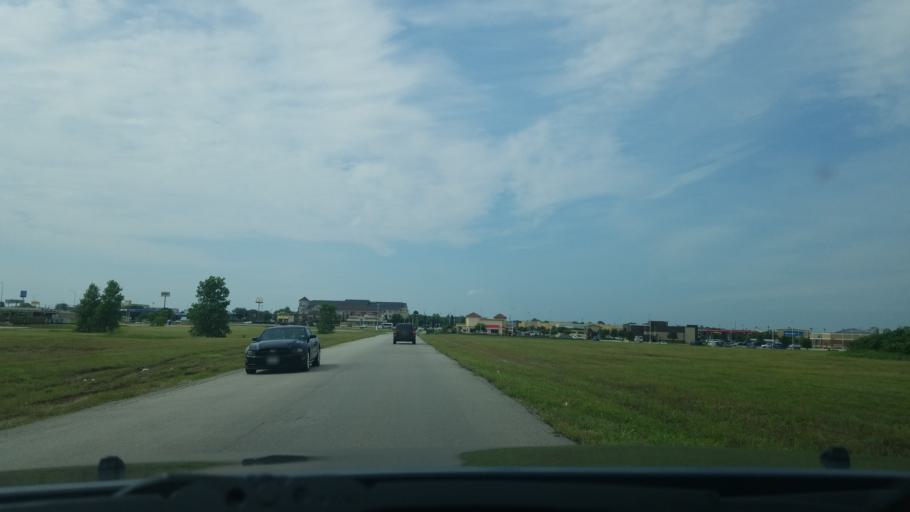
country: US
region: Texas
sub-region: Denton County
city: Denton
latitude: 33.2267
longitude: -97.1712
